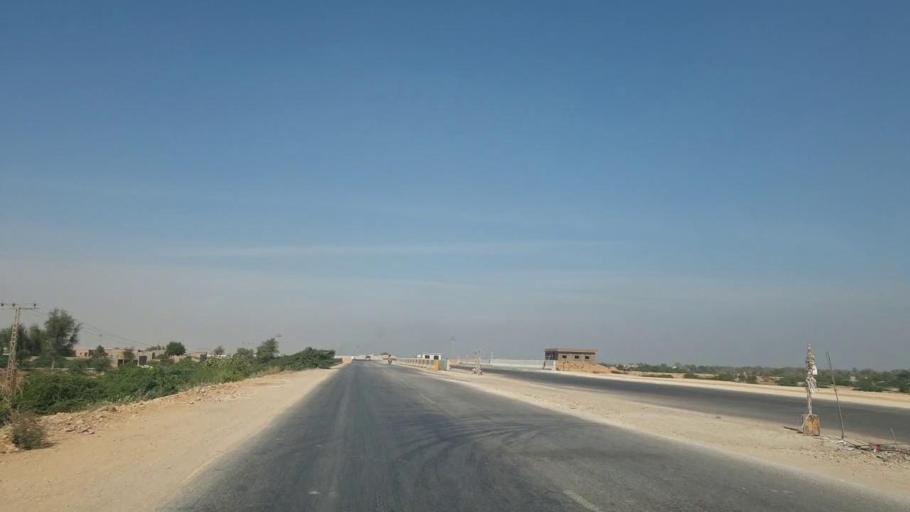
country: PK
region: Sindh
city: Matiari
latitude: 25.6524
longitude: 68.3008
